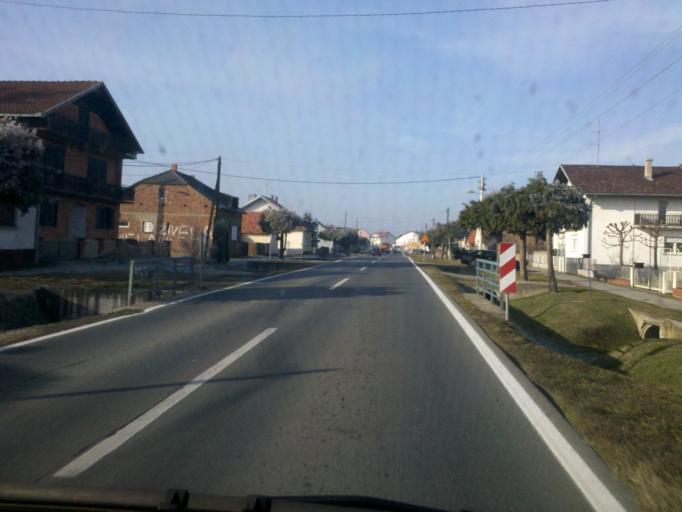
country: HR
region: Koprivnicko-Krizevacka
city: Kalinovac
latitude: 45.9815
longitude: 17.1610
